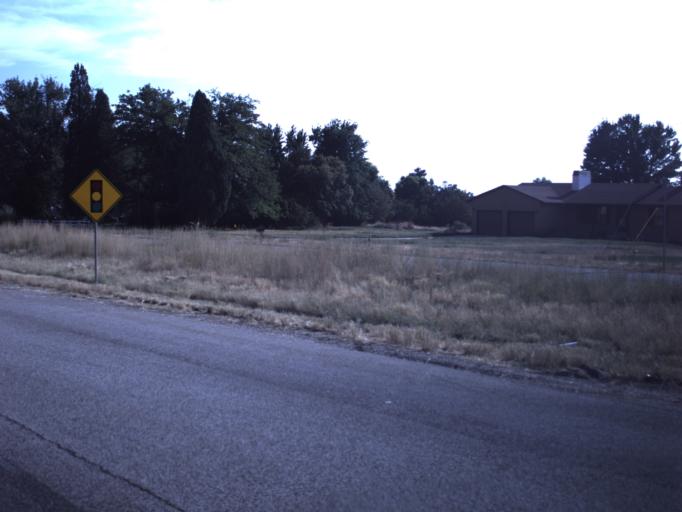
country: US
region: Utah
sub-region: Davis County
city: Fruit Heights
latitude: 41.0440
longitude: -111.9100
